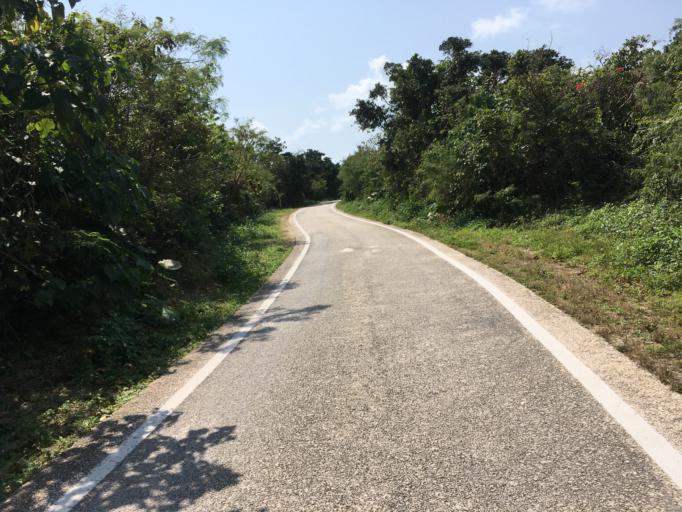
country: JP
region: Okinawa
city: Ishigaki
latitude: 24.3227
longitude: 124.0806
